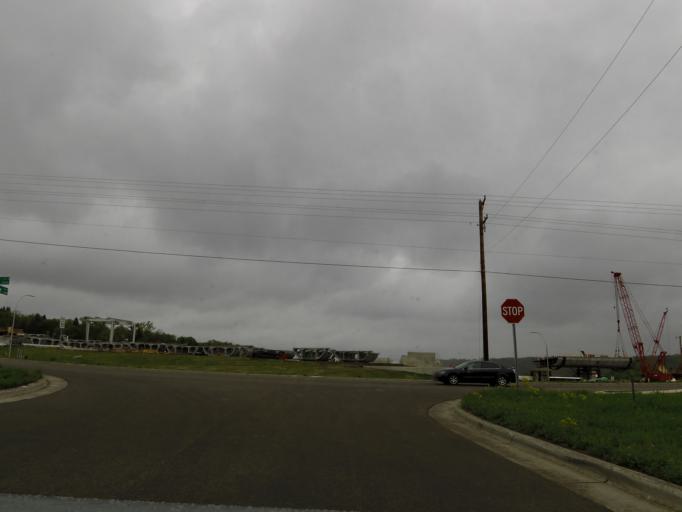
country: US
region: Minnesota
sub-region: Washington County
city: Oak Park Heights
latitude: 45.0343
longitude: -92.7933
